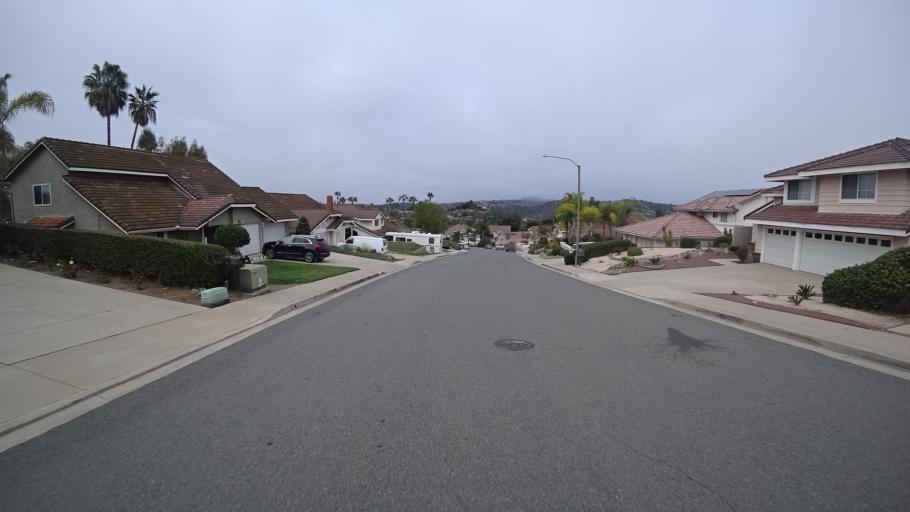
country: US
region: California
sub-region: San Diego County
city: Rancho San Diego
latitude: 32.7533
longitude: -116.9138
